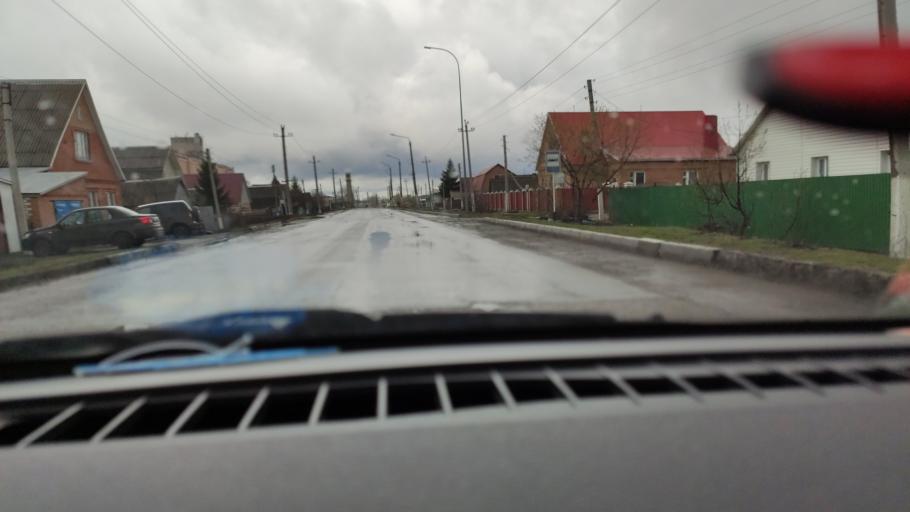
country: RU
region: Tatarstan
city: Nurlat
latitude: 54.4288
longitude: 50.8211
